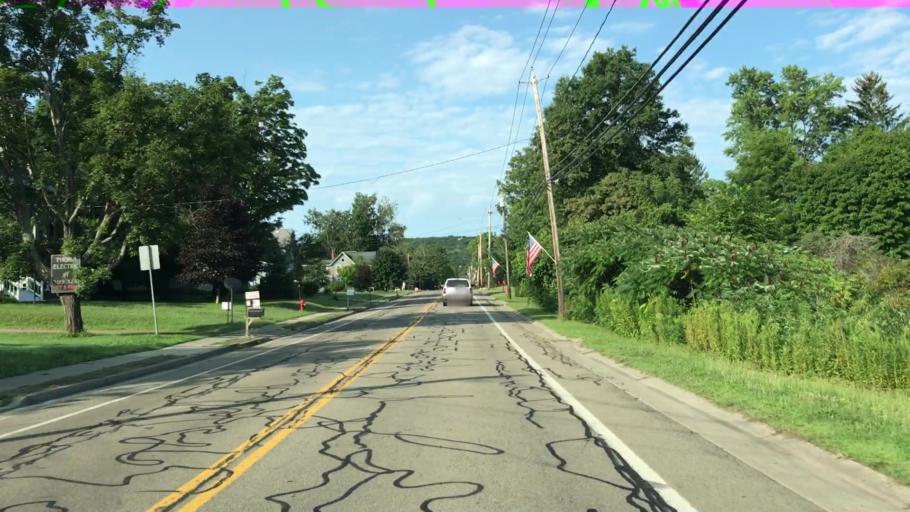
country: US
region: New York
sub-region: Chautauqua County
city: Fredonia
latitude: 42.3415
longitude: -79.3145
